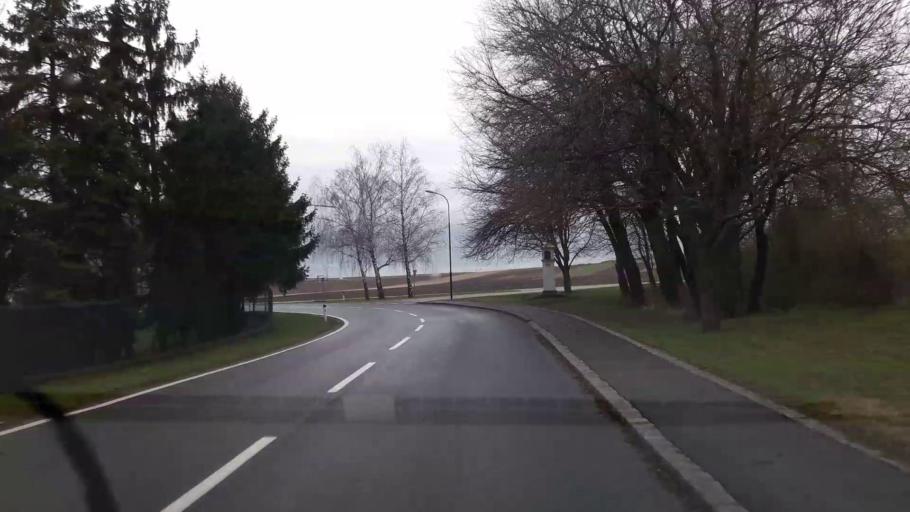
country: AT
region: Lower Austria
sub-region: Politischer Bezirk Bruck an der Leitha
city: Scharndorf
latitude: 48.0913
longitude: 16.7978
